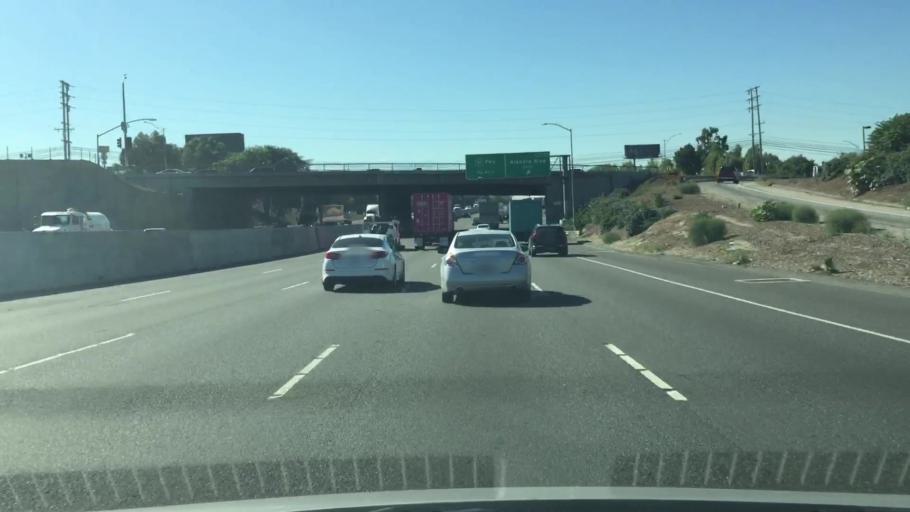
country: US
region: California
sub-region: Los Angeles County
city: East Rancho Dominguez
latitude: 33.8901
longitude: -118.1891
